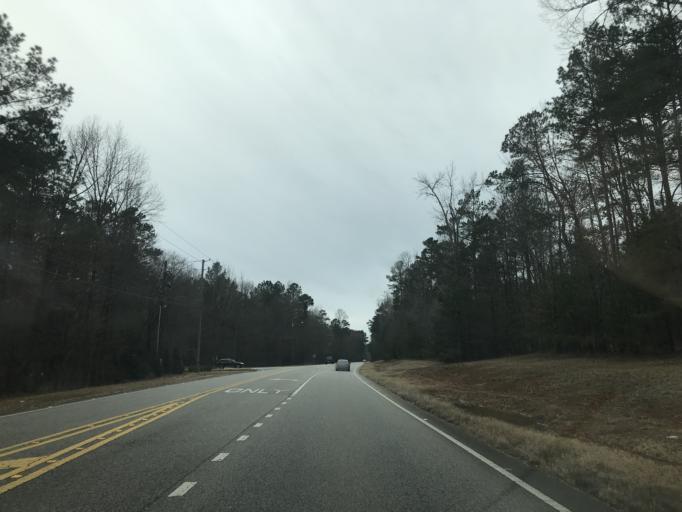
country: US
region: Alabama
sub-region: Shelby County
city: Brook Highland
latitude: 33.4542
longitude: -86.6498
